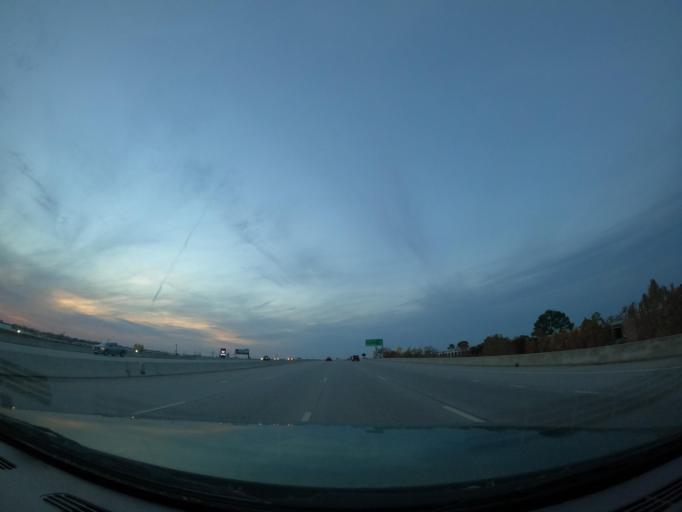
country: US
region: Oklahoma
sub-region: Tulsa County
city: Broken Arrow
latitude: 36.1008
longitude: -95.8664
